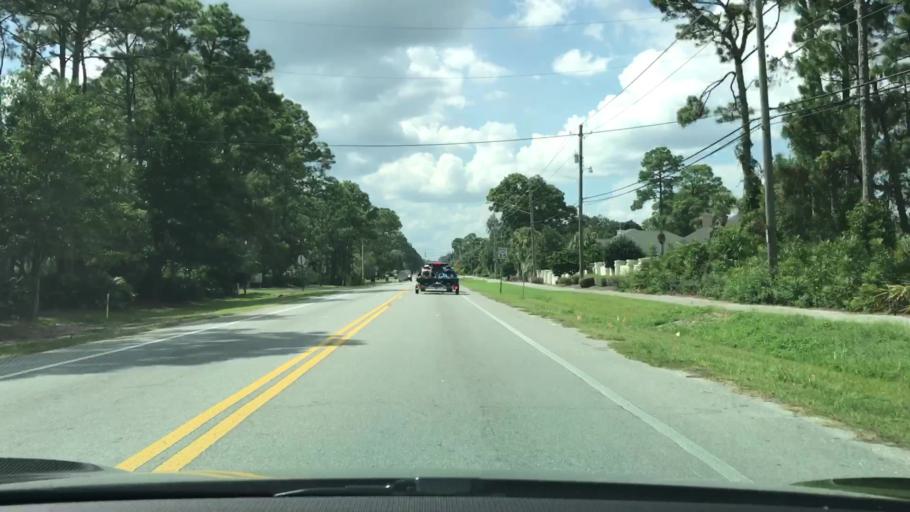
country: US
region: Florida
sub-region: Bay County
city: Lower Grand Lagoon
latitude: 30.1640
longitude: -85.7719
